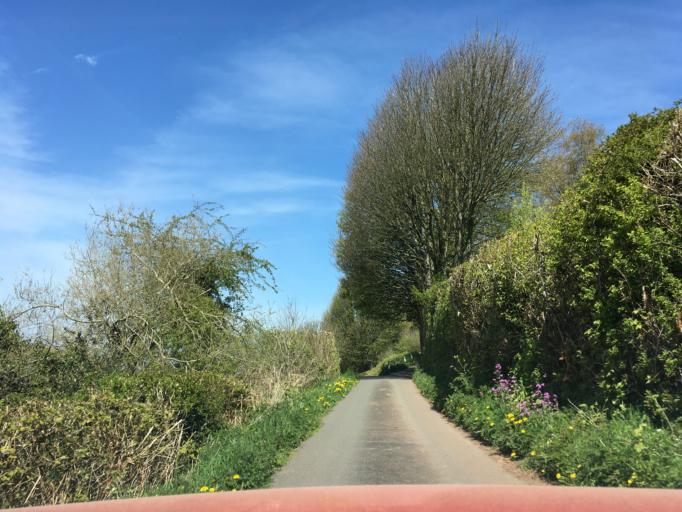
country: GB
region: Wales
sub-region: Monmouthshire
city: Llangwm
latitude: 51.6829
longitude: -2.8115
